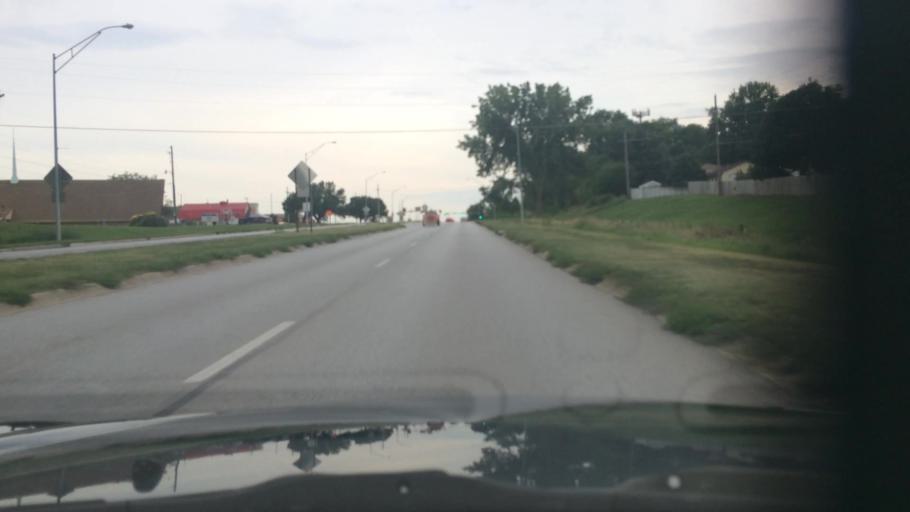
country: US
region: Nebraska
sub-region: Douglas County
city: Ralston
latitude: 41.1940
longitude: -96.0431
